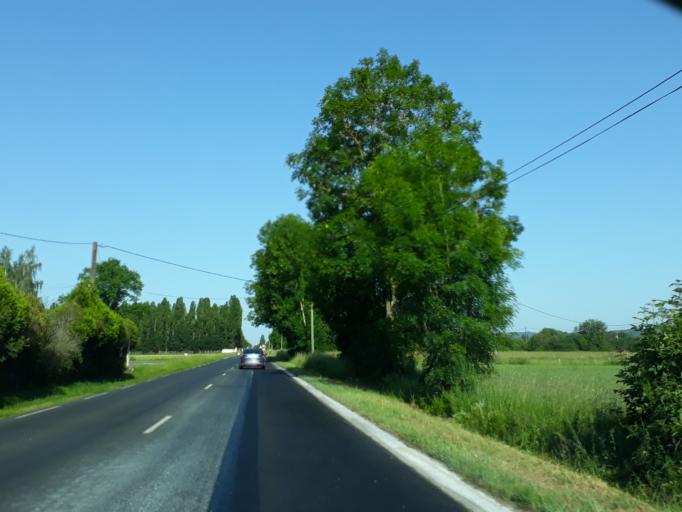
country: FR
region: Limousin
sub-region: Departement de la Correze
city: Larche
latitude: 45.1256
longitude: 1.3918
